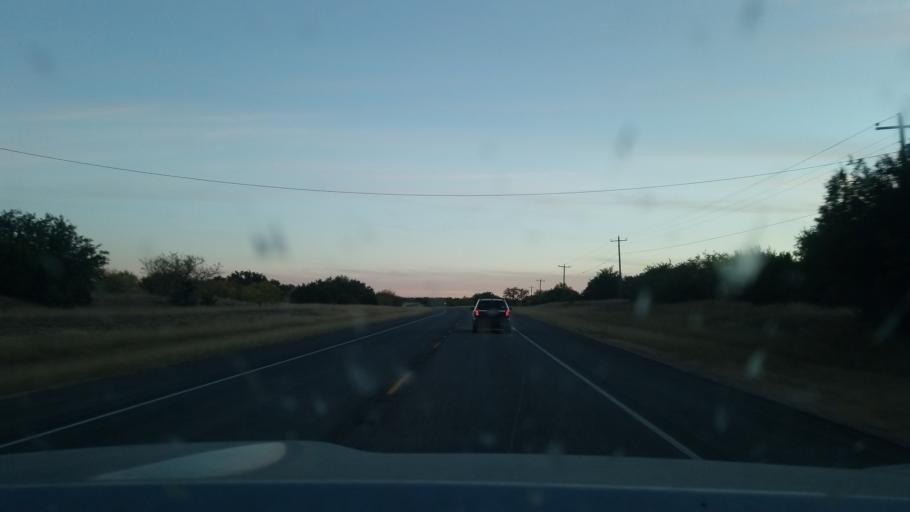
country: US
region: Texas
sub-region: Stephens County
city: Breckenridge
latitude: 32.5845
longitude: -98.8972
